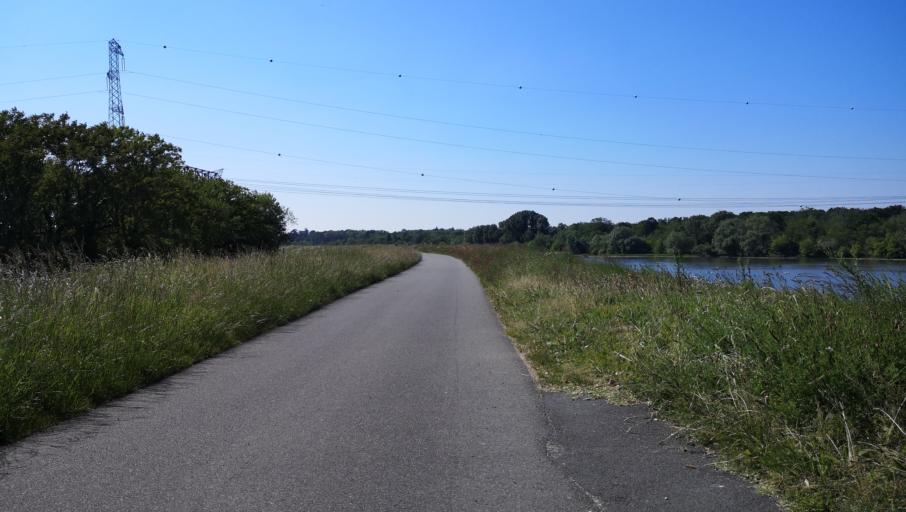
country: FR
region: Centre
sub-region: Departement du Loiret
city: Mareau-aux-Pres
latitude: 47.8629
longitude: 1.7981
